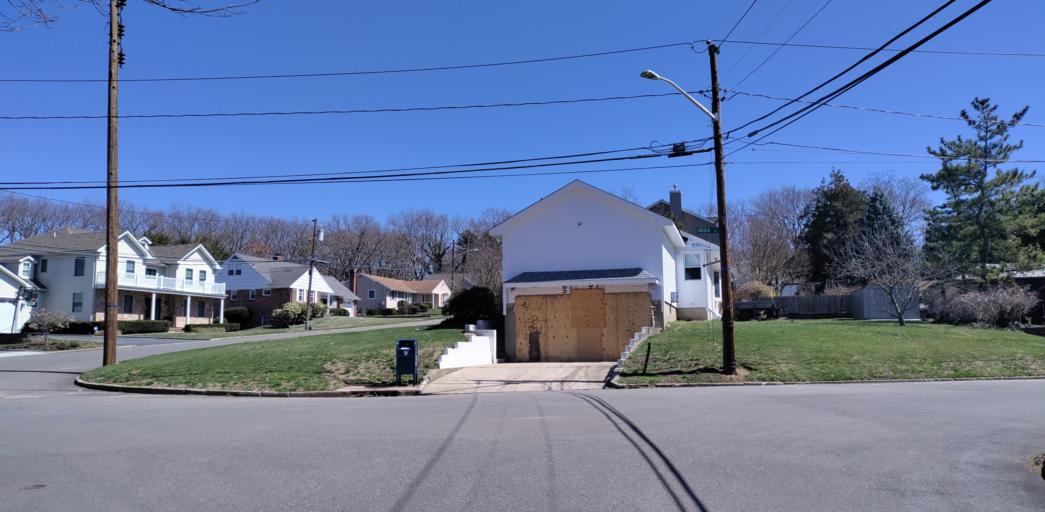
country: US
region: New York
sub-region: Nassau County
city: Glenwood Landing
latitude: 40.8240
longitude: -73.6361
